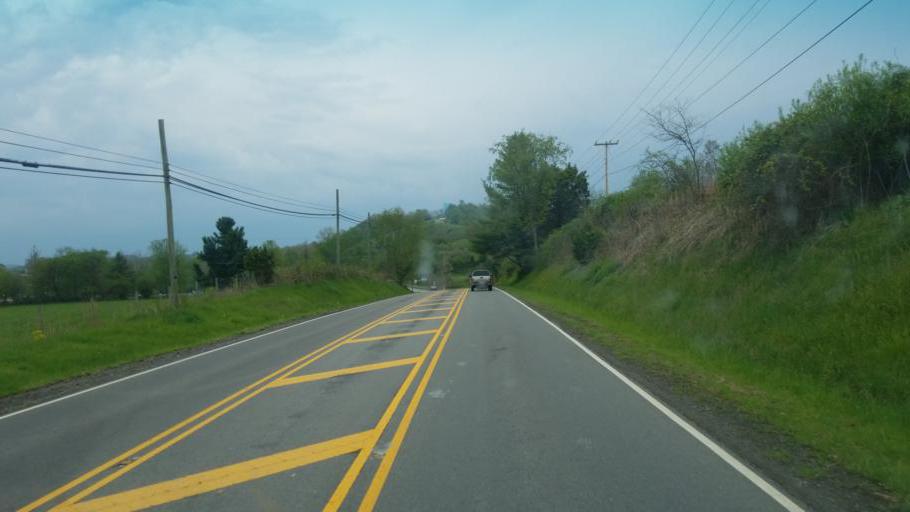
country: US
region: Virginia
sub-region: Smyth County
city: Chilhowie
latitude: 36.8141
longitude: -81.6586
